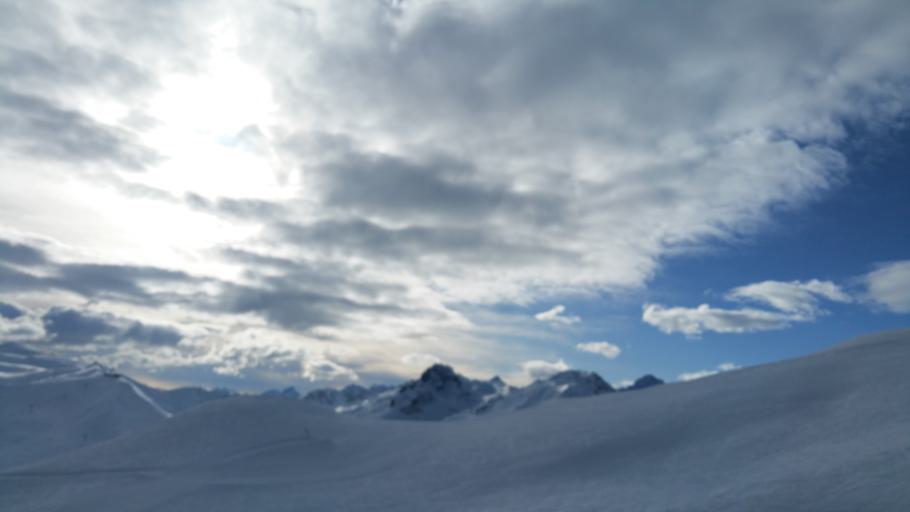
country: FR
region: Rhone-Alpes
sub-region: Departement de la Savoie
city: Saint-Etienne-de-Cuines
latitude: 45.2721
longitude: 6.2586
